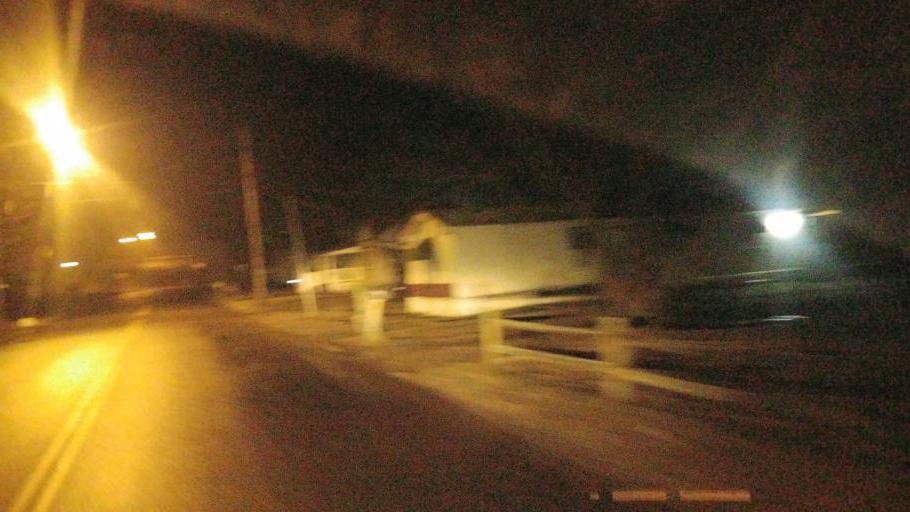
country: US
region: Ohio
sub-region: Holmes County
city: Millersburg
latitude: 40.4905
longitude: -81.9842
